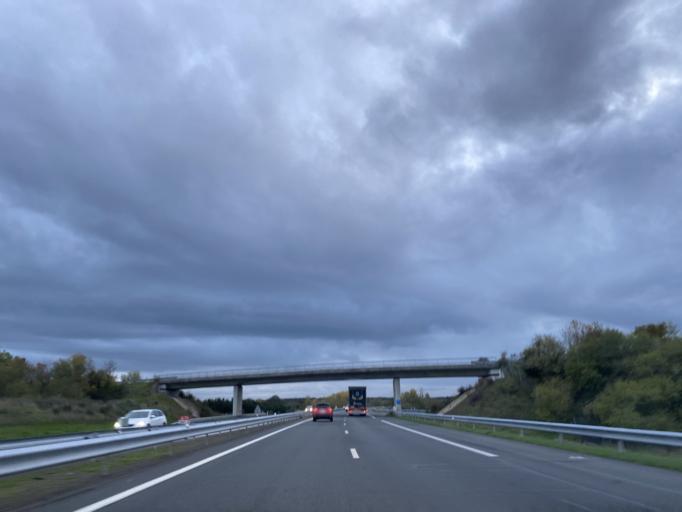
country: FR
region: Centre
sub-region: Departement du Cher
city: Orval
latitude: 46.7928
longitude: 2.4135
